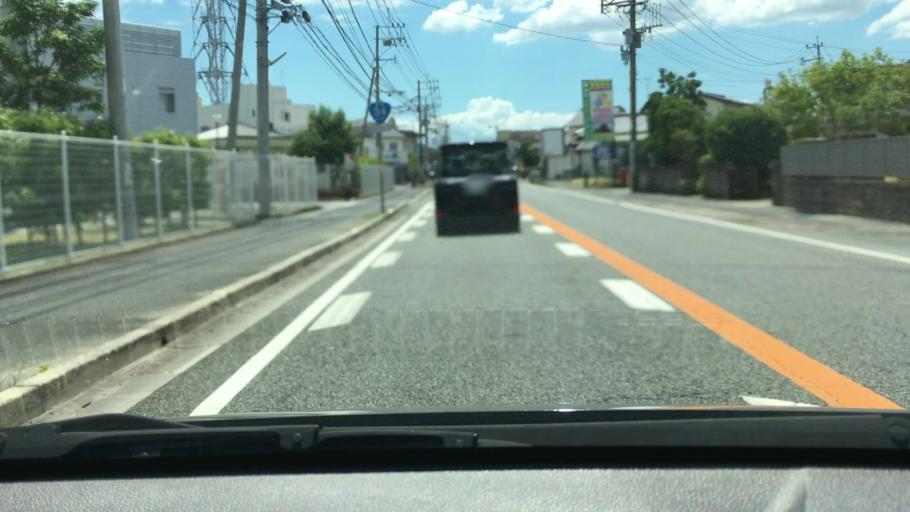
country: JP
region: Saga Prefecture
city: Kanzakimachi-kanzaki
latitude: 33.3144
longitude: 130.3768
